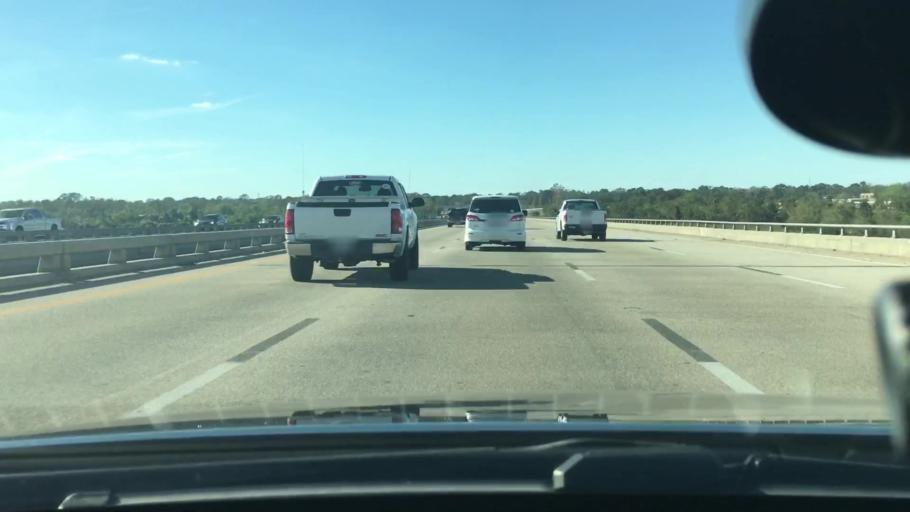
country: US
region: North Carolina
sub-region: Craven County
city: New Bern
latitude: 35.0970
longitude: -77.0472
